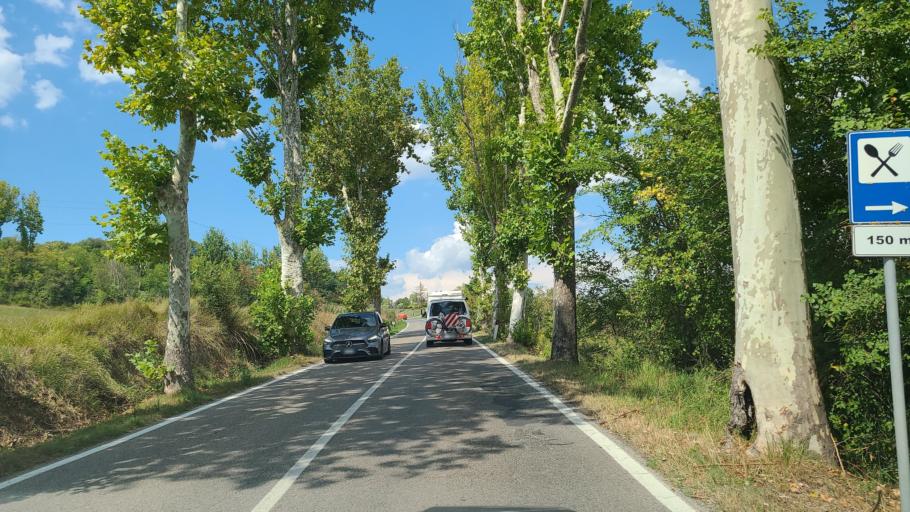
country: IT
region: Tuscany
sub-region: Provincia di Siena
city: Colle di Val d'Elsa
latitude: 43.4113
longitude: 11.0647
